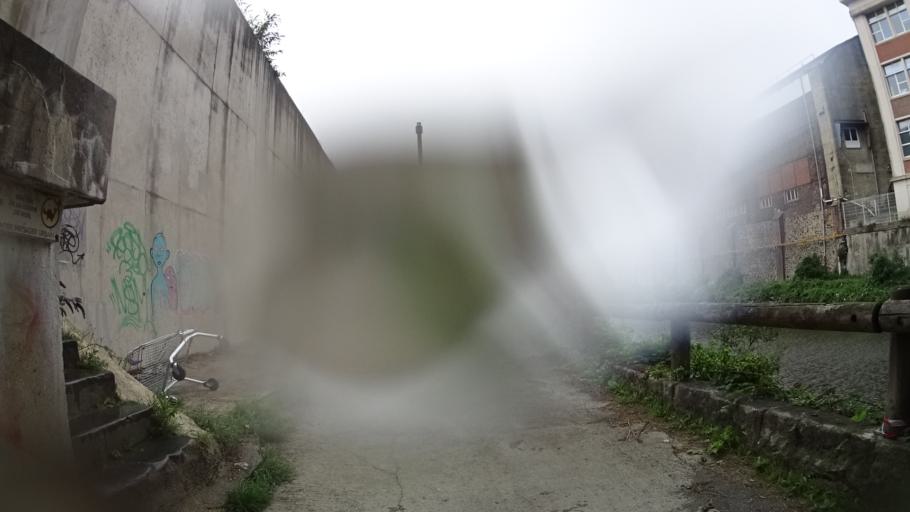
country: FR
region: Nord-Pas-de-Calais
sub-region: Departement du Nord
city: Louvroil
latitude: 50.2667
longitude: 3.9555
